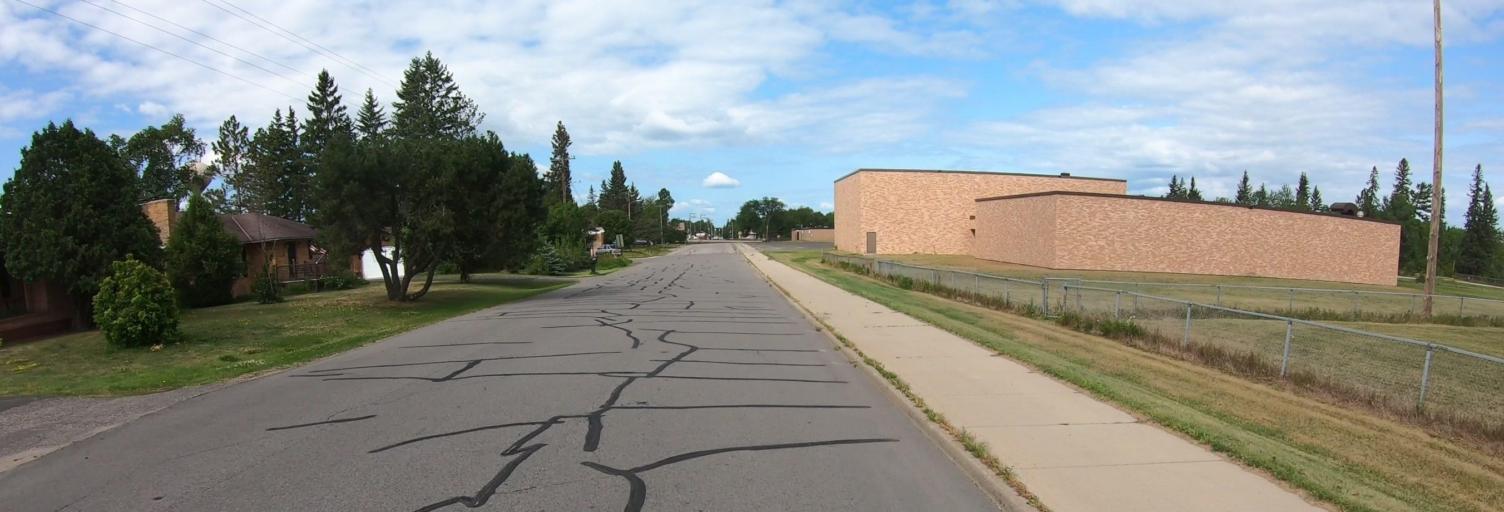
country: US
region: Minnesota
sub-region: Saint Louis County
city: Mountain Iron
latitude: 47.8538
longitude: -92.6814
